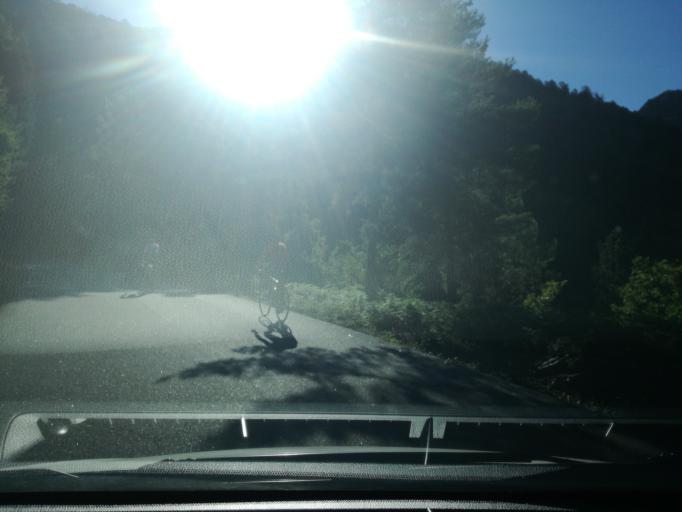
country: PT
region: Braga
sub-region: Vieira do Minho
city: Real
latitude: 41.7494
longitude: -8.1533
